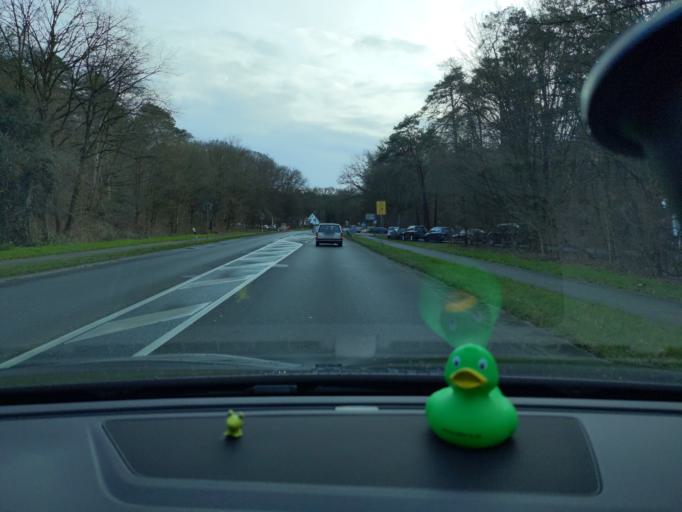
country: DE
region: North Rhine-Westphalia
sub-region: Regierungsbezirk Koln
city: Eil
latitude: 50.9009
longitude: 7.1003
